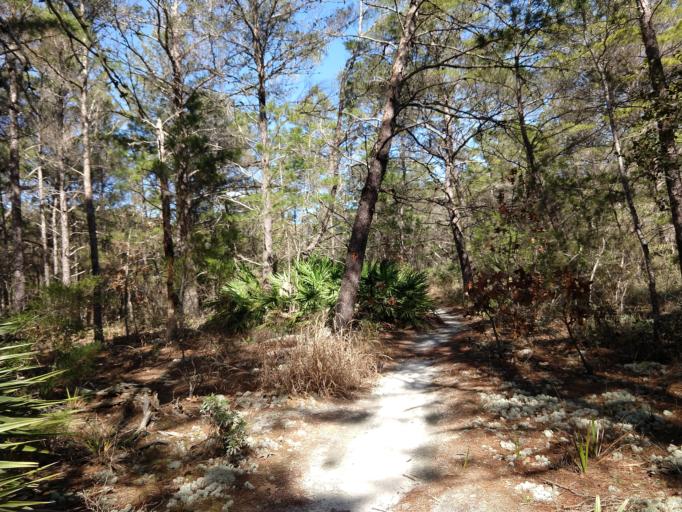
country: US
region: Florida
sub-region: Walton County
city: Seaside
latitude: 30.3459
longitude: -86.1998
